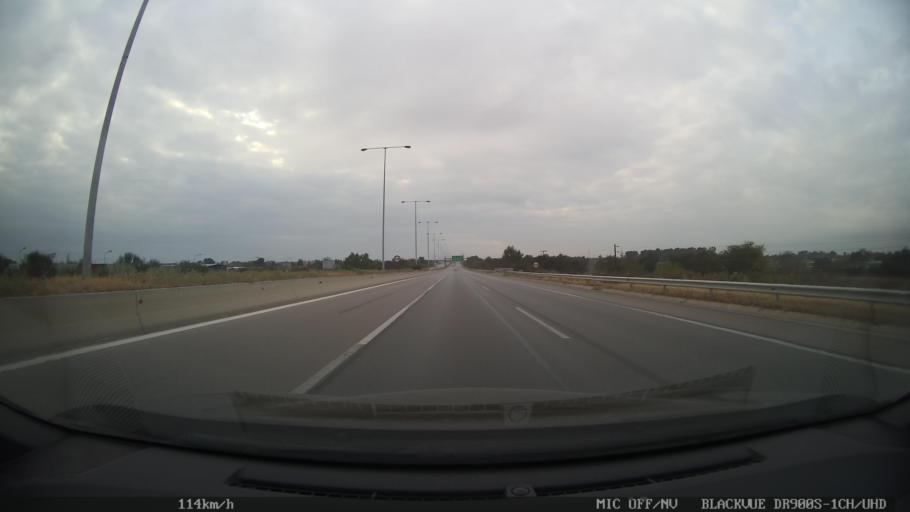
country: GR
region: Central Macedonia
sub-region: Nomos Thessalonikis
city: Nea Magnisia
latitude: 40.6647
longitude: 22.8367
